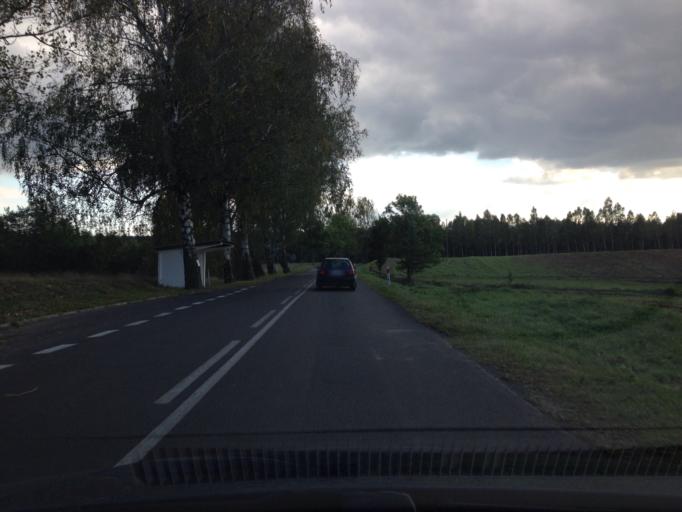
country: PL
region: Kujawsko-Pomorskie
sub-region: Powiat rypinski
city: Rogowo
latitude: 52.9918
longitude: 19.3423
